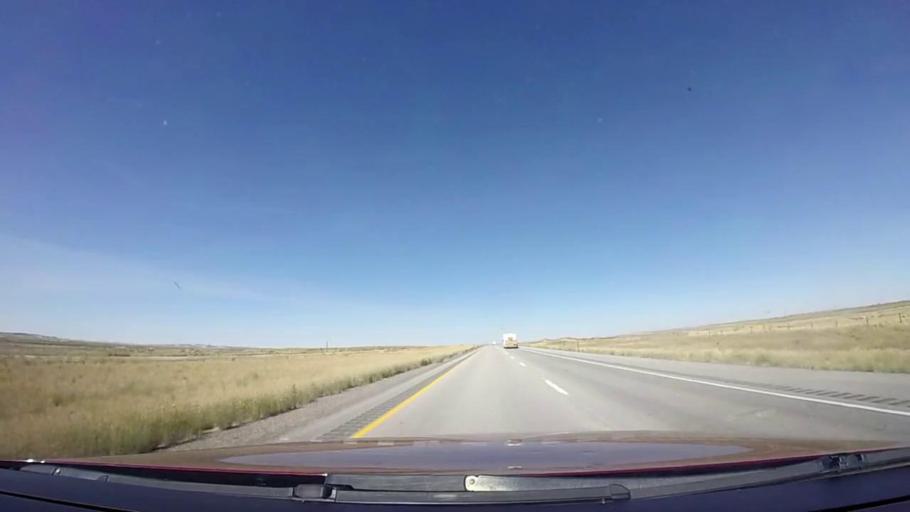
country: US
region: Wyoming
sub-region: Sweetwater County
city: Rock Springs
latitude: 41.6313
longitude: -108.3333
